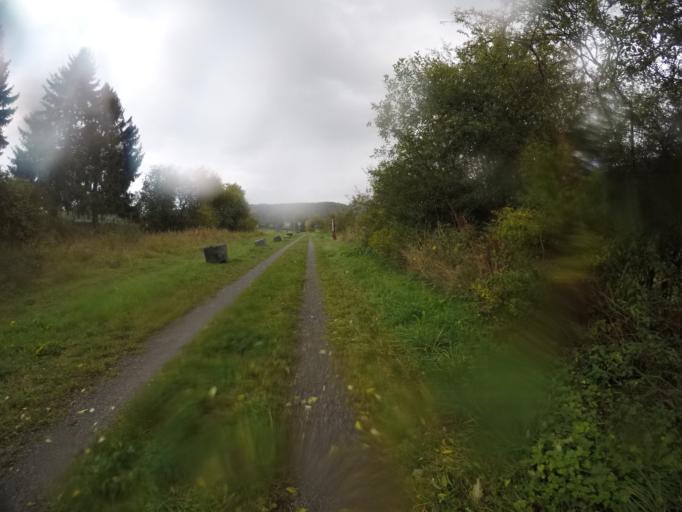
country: BE
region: Wallonia
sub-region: Province du Luxembourg
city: Fauvillers
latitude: 49.8755
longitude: 5.6784
